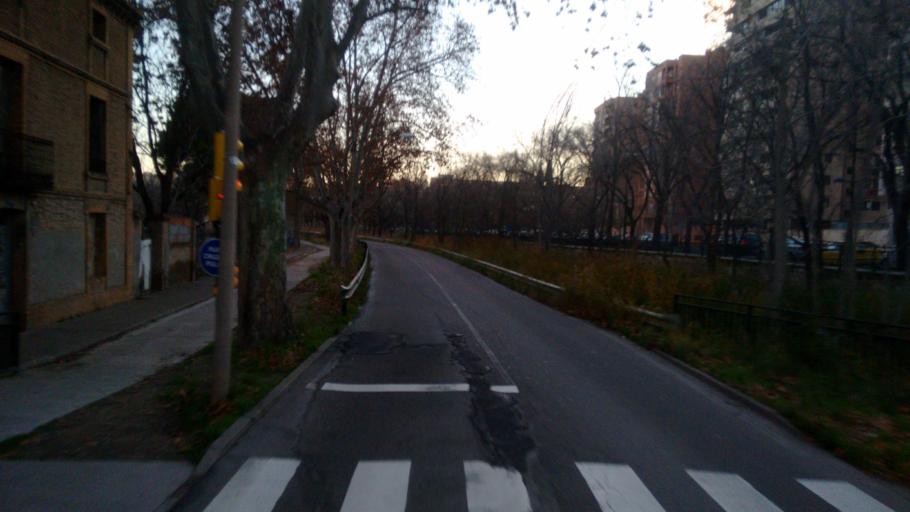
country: ES
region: Aragon
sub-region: Provincia de Zaragoza
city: Zaragoza
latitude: 41.6319
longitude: -0.8813
